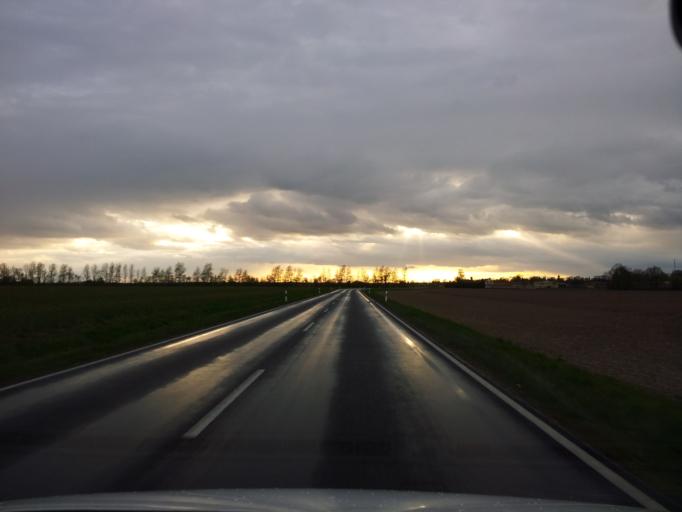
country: DE
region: Brandenburg
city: Dahme
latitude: 51.8611
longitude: 13.4542
